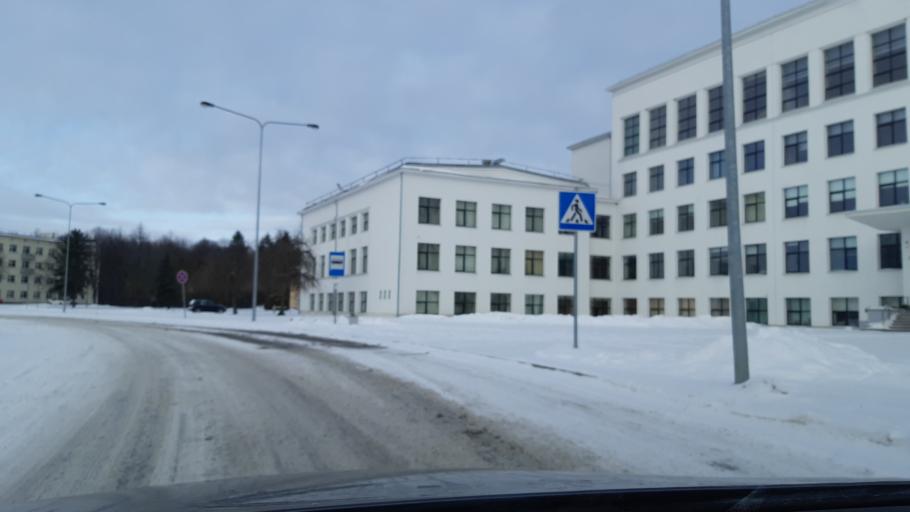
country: LT
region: Kauno apskritis
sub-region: Kauno rajonas
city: Akademija (Kaunas)
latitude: 54.8934
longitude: 23.8351
